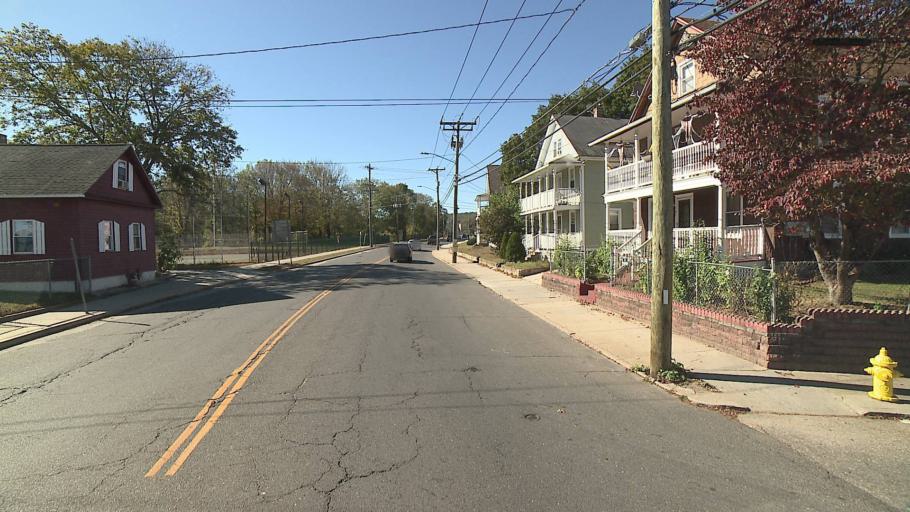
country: US
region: Connecticut
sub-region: Windham County
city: Willimantic
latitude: 41.7147
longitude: -72.1991
